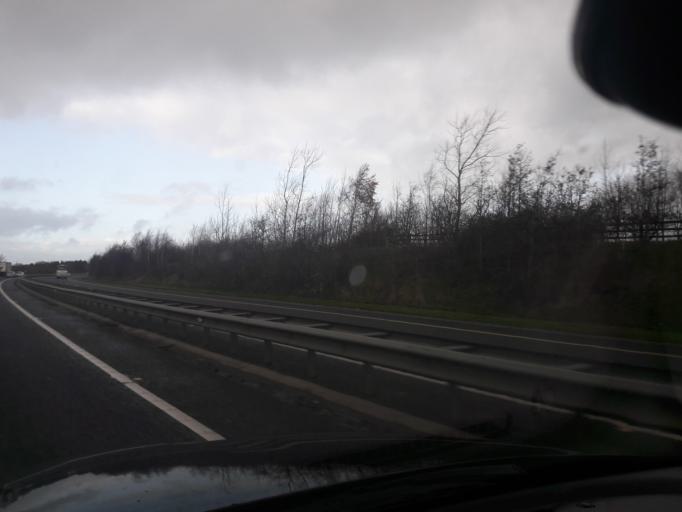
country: IE
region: Leinster
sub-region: An Mhi
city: Ashbourne
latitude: 53.4932
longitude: -6.4122
